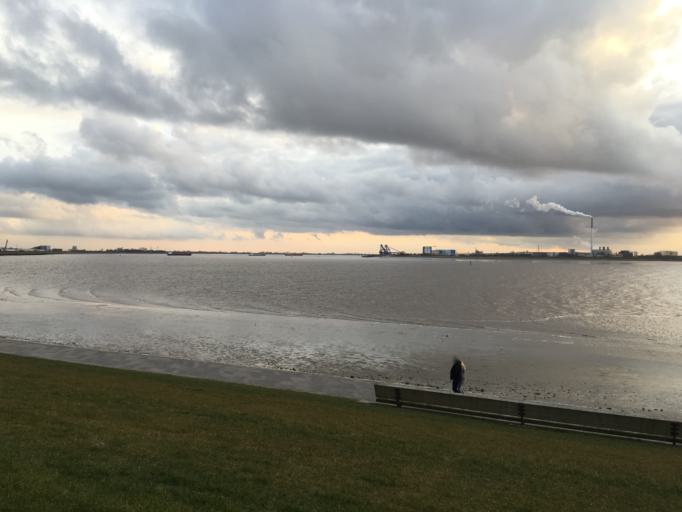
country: DE
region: Bremen
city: Bremerhaven
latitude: 53.5429
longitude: 8.5732
